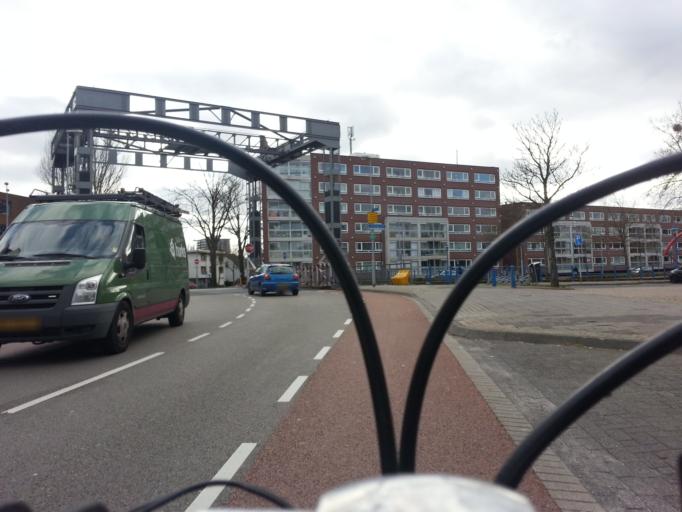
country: NL
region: North Brabant
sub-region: Gemeente Eindhoven
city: Villapark
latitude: 51.4372
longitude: 5.4906
